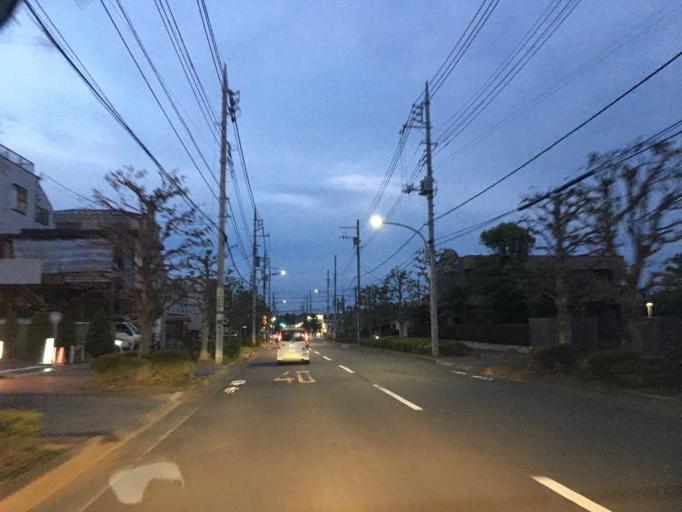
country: JP
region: Tokyo
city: Higashimurayama-shi
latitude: 35.7319
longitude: 139.4526
